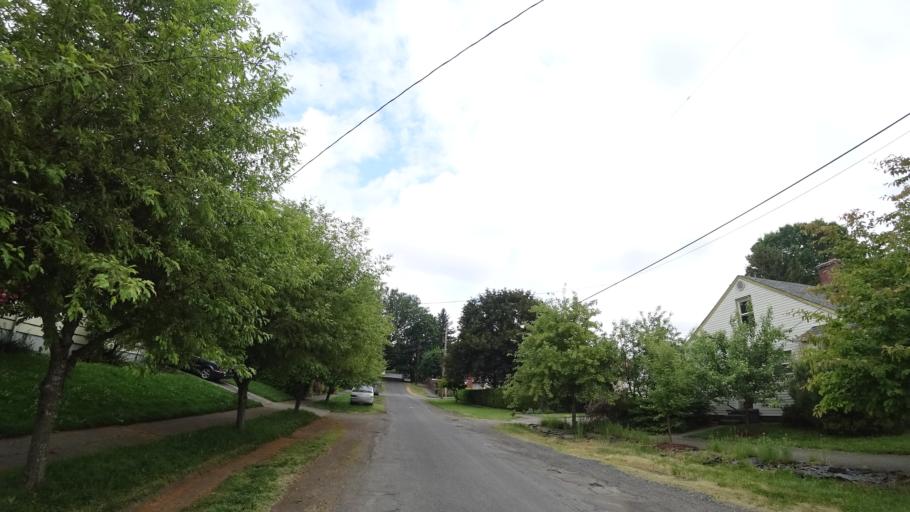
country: US
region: Oregon
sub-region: Multnomah County
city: Portland
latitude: 45.4992
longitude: -122.6286
